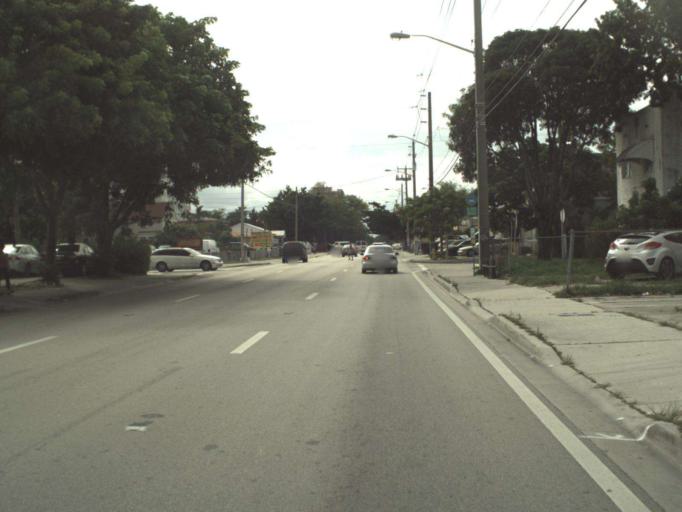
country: US
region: Florida
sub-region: Miami-Dade County
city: Miami
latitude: 25.7664
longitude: -80.2284
